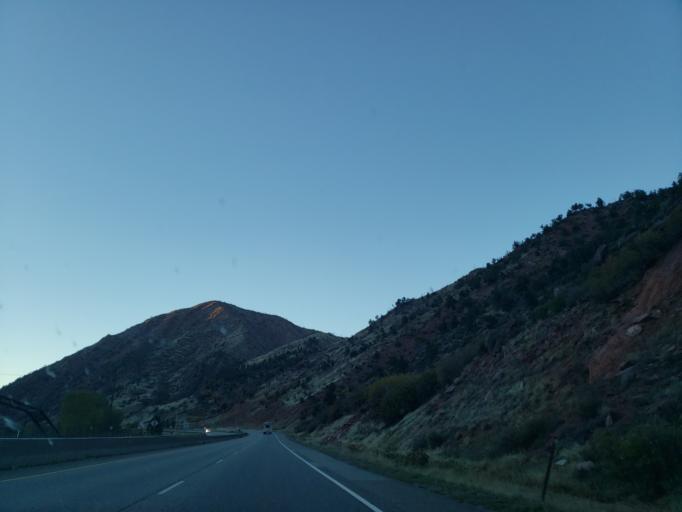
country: US
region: Colorado
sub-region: Garfield County
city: Glenwood Springs
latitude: 39.5614
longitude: -107.4061
